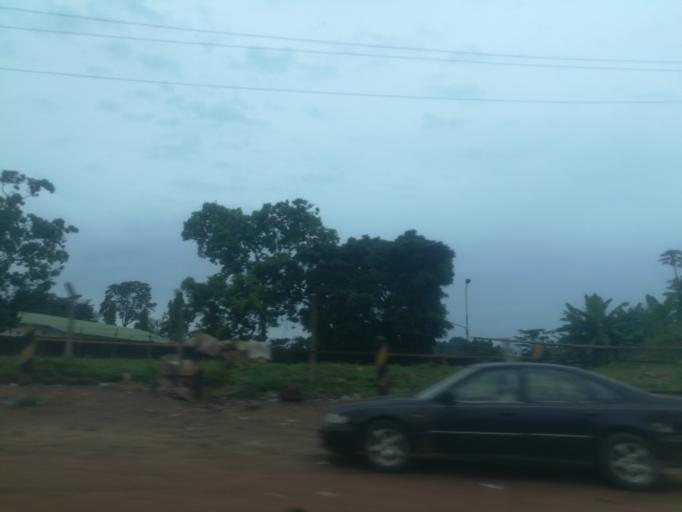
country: NG
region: Oyo
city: Ibadan
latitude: 7.3925
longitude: 3.9717
